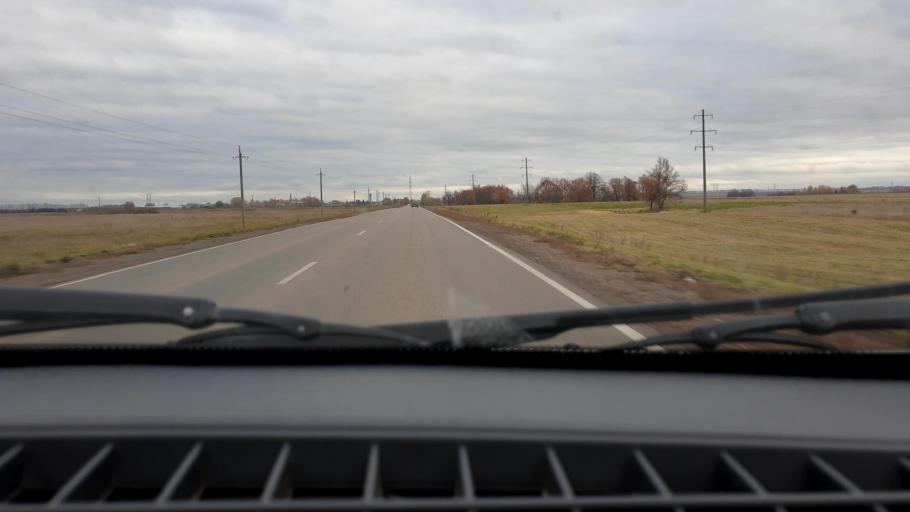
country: RU
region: Bashkortostan
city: Kabakovo
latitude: 54.5587
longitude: 56.0108
